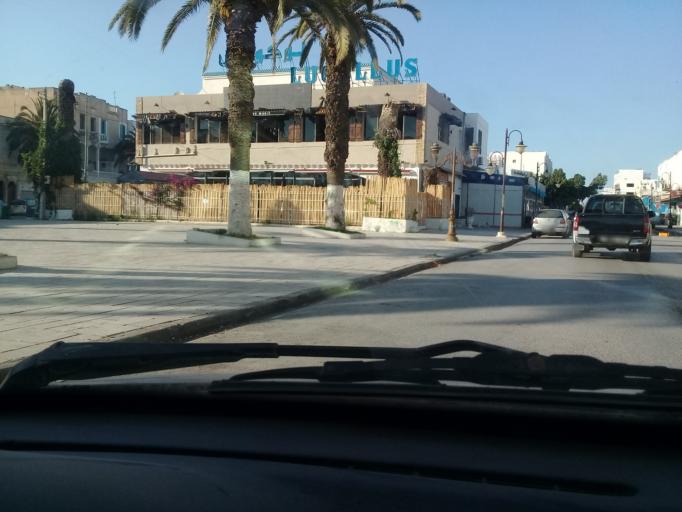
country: TN
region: Tunis
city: La Goulette
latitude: 36.8167
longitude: 10.3051
